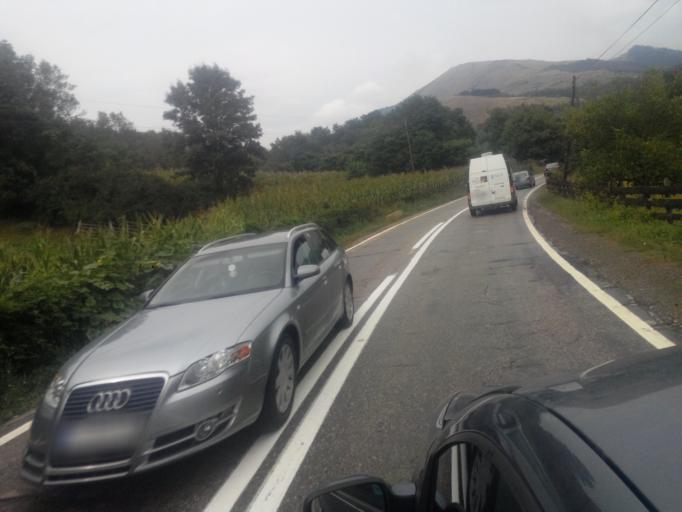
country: RO
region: Alba
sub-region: Comuna Ocolis
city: Ocolis
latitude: 46.4647
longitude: 23.4731
